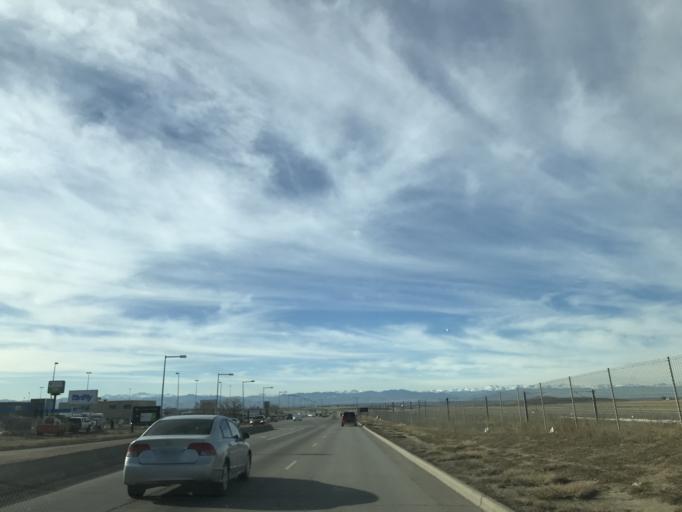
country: US
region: Colorado
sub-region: Adams County
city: Aurora
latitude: 39.8382
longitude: -104.7103
